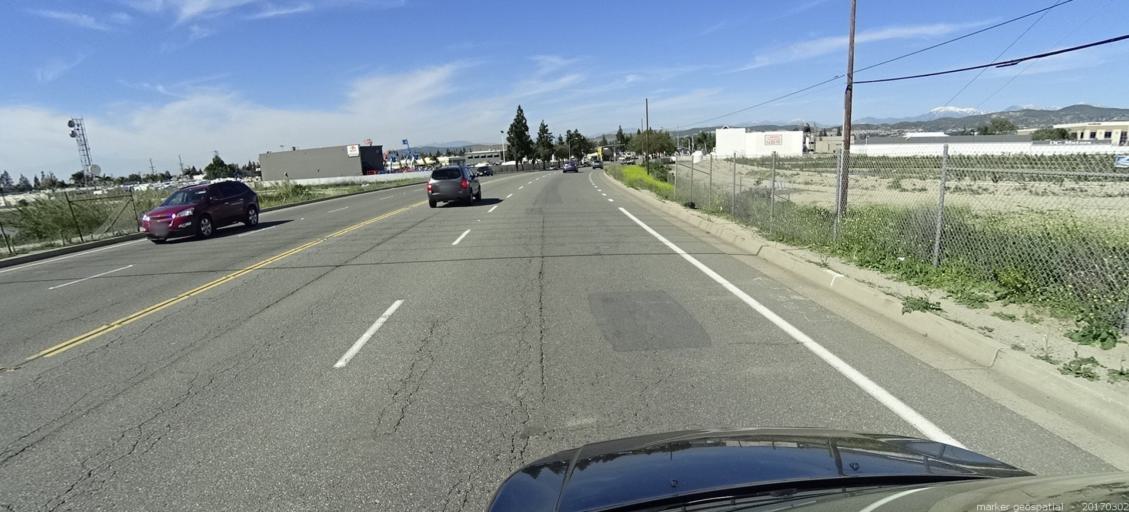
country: US
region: California
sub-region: Orange County
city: Yorba Linda
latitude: 33.8572
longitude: -117.8179
